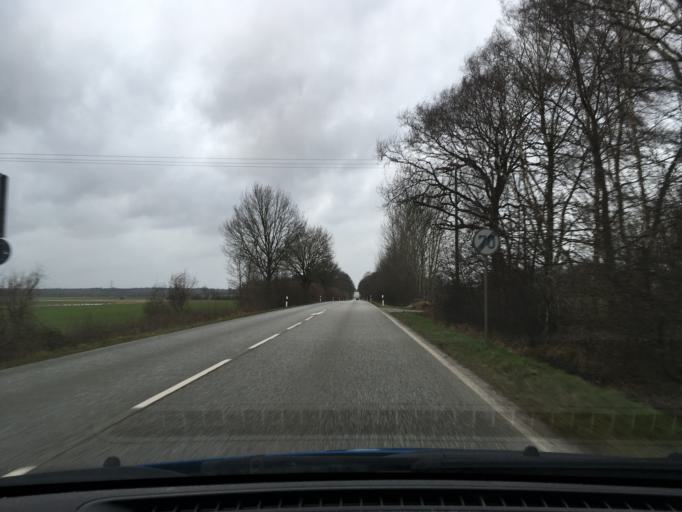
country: DE
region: Schleswig-Holstein
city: Wangelau
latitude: 53.4565
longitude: 10.5496
